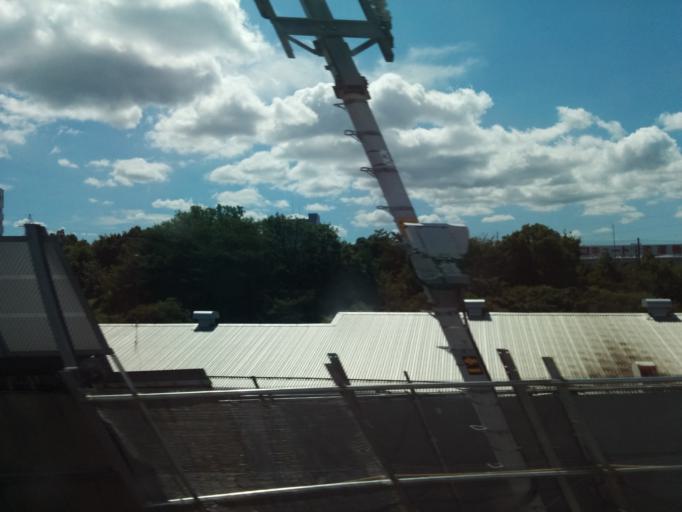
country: JP
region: Shiga Prefecture
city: Kusatsu
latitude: 34.9904
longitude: 135.9516
